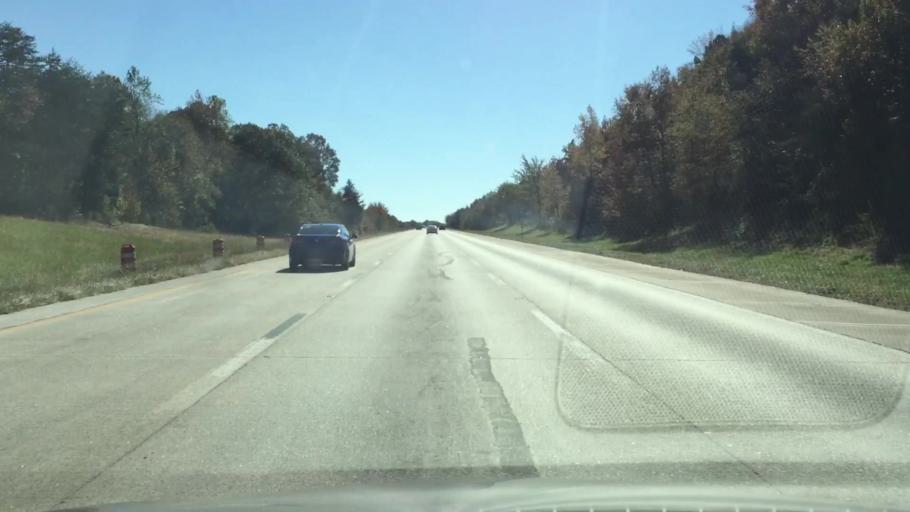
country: US
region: North Carolina
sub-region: Guilford County
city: Jamestown
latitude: 35.9709
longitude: -79.8921
